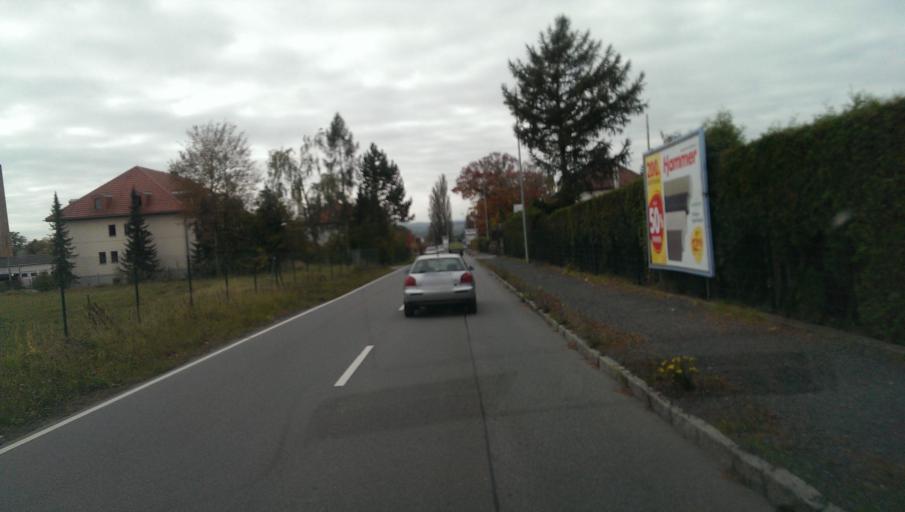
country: DE
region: Saxony
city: Pirna
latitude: 50.9777
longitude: 13.9440
